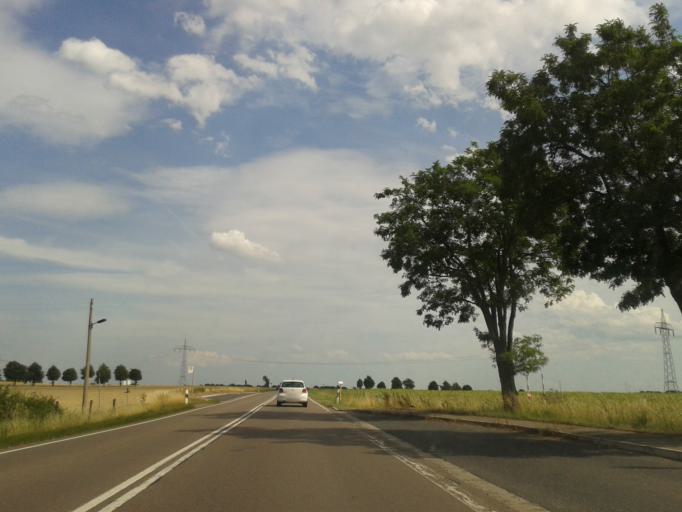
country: DE
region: Saxony
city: Wilsdruff
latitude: 51.0470
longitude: 13.5570
